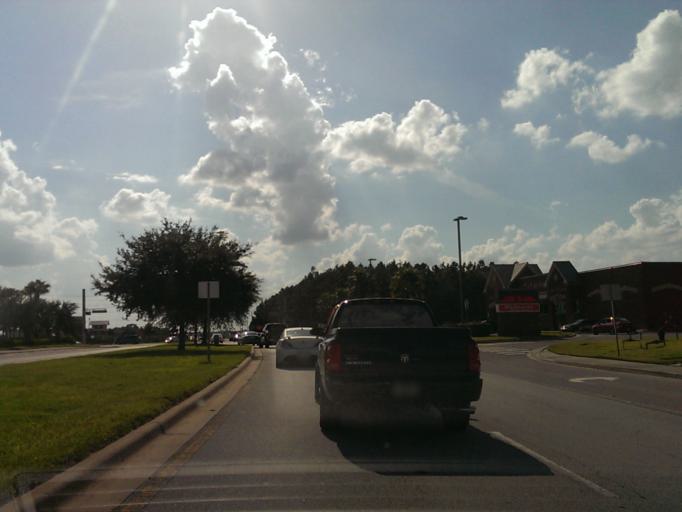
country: US
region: Florida
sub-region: Orange County
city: Oakland
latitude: 28.5179
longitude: -81.6188
